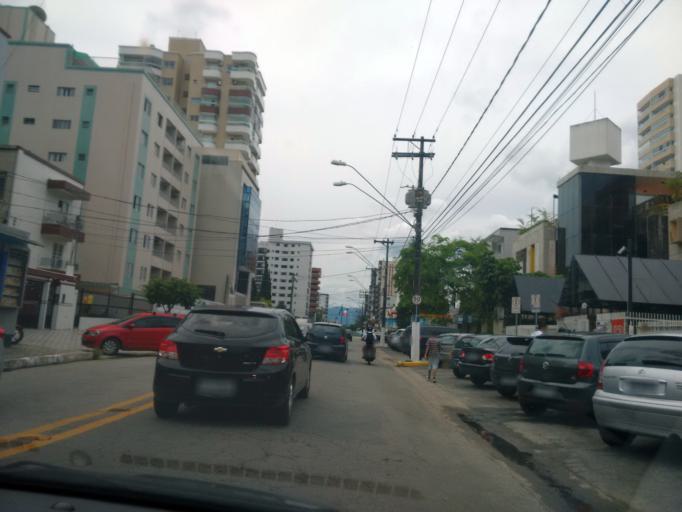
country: BR
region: Sao Paulo
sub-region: Praia Grande
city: Praia Grande
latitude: -24.0116
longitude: -46.4207
